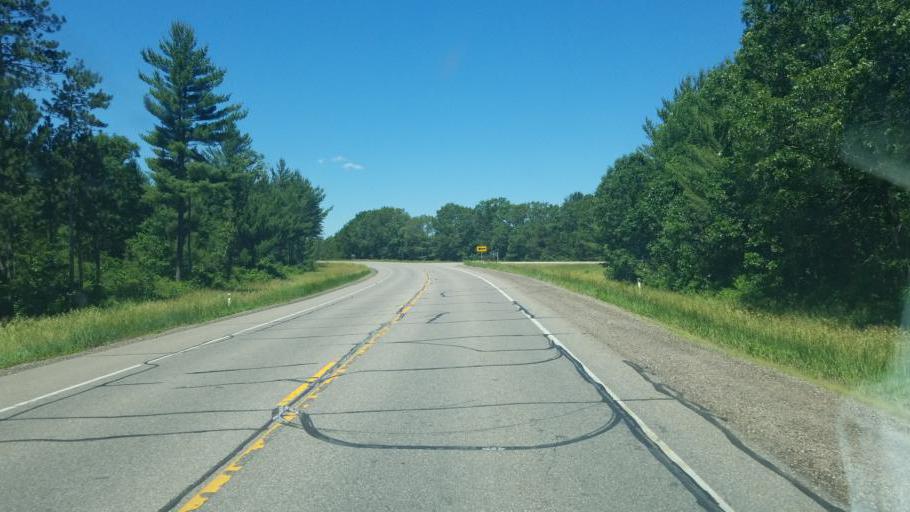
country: US
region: Wisconsin
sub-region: Adams County
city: Friendship
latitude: 44.0457
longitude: -89.9704
